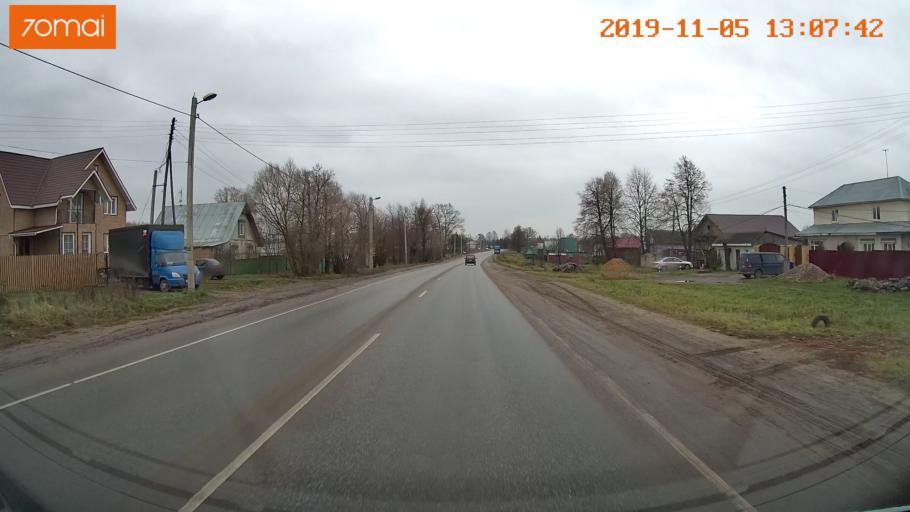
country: RU
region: Ivanovo
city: Kitovo
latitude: 56.8665
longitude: 41.2839
